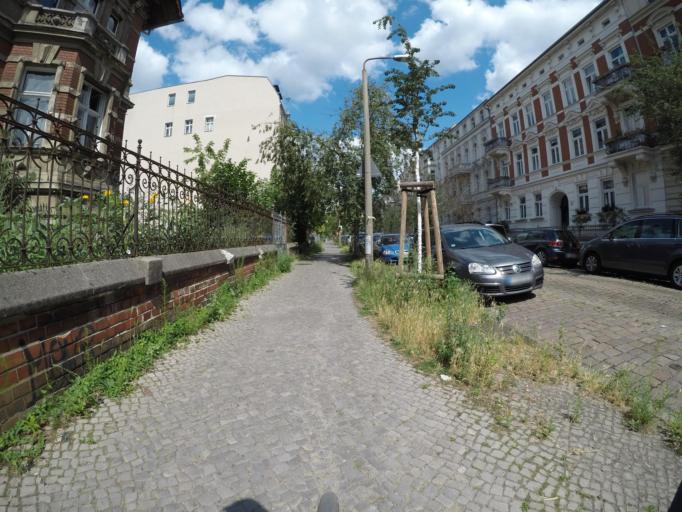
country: DE
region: Brandenburg
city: Potsdam
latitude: 52.3945
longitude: 13.0343
